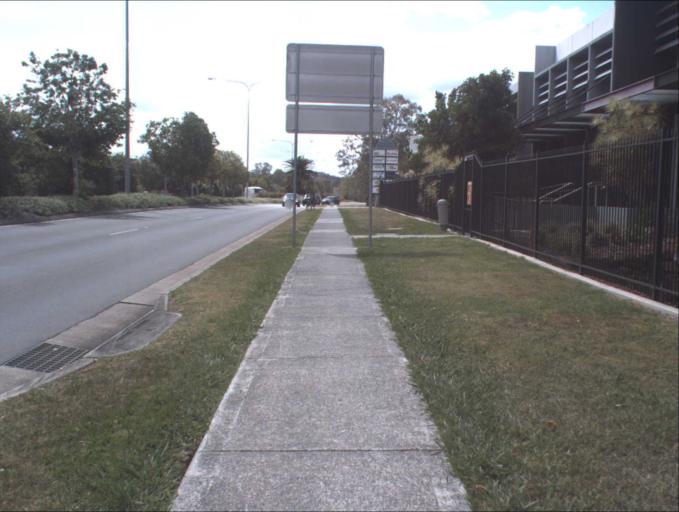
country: AU
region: Queensland
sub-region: Logan
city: Slacks Creek
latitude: -27.6638
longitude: 153.1414
